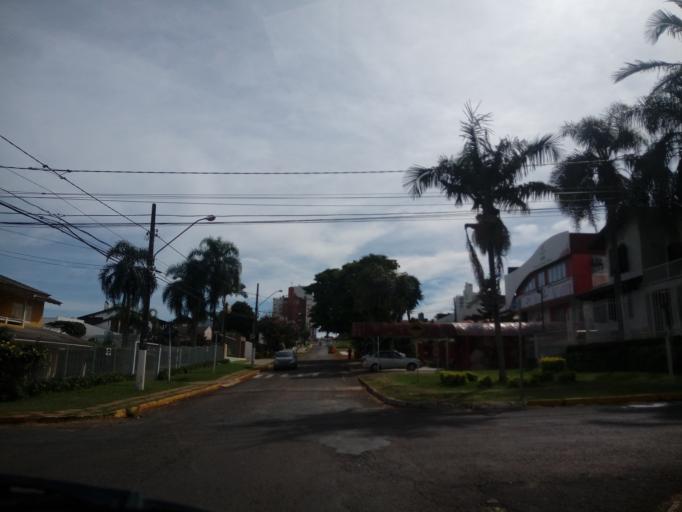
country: BR
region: Santa Catarina
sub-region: Chapeco
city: Chapeco
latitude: -27.1148
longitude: -52.6151
